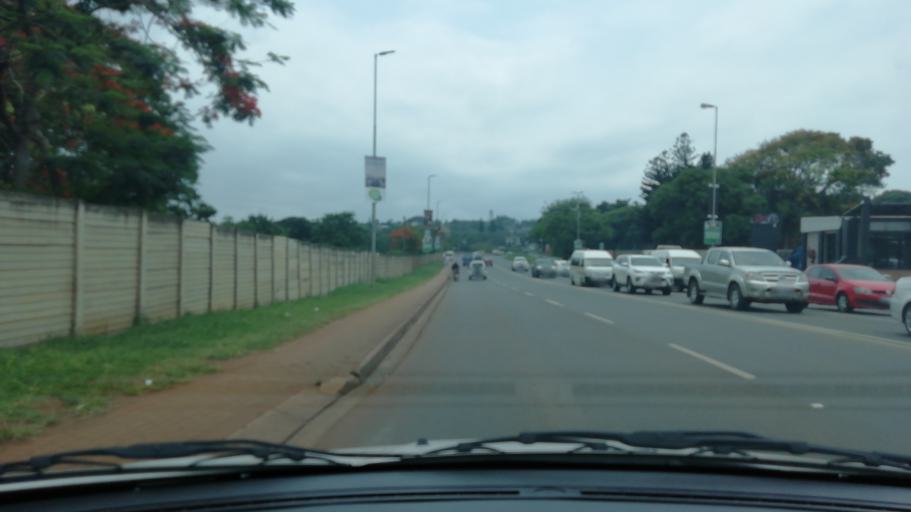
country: ZA
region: KwaZulu-Natal
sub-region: uThungulu District Municipality
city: Empangeni
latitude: -28.7585
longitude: 31.9011
